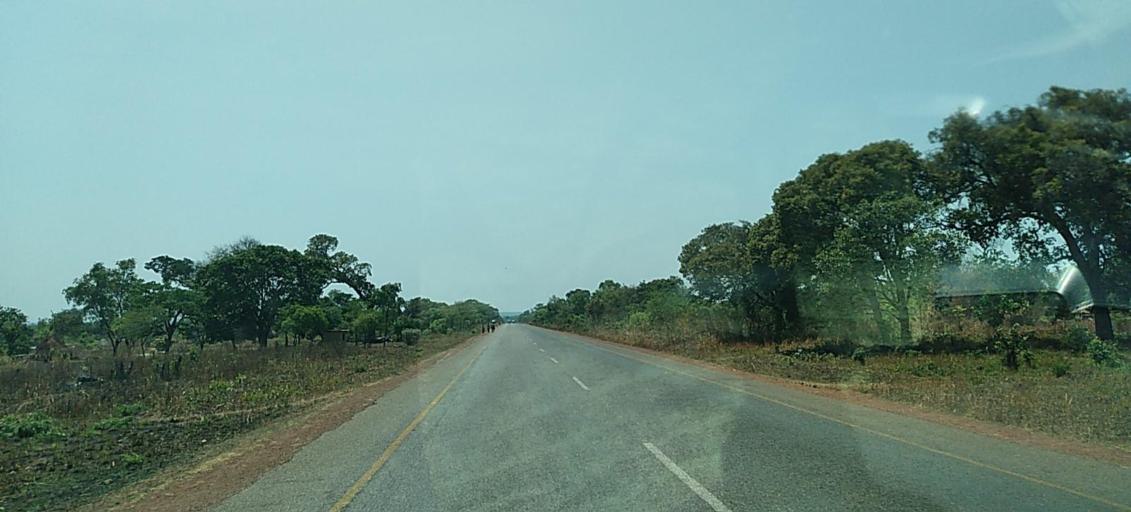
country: ZM
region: North-Western
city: Solwezi
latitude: -12.3933
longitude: 26.2175
